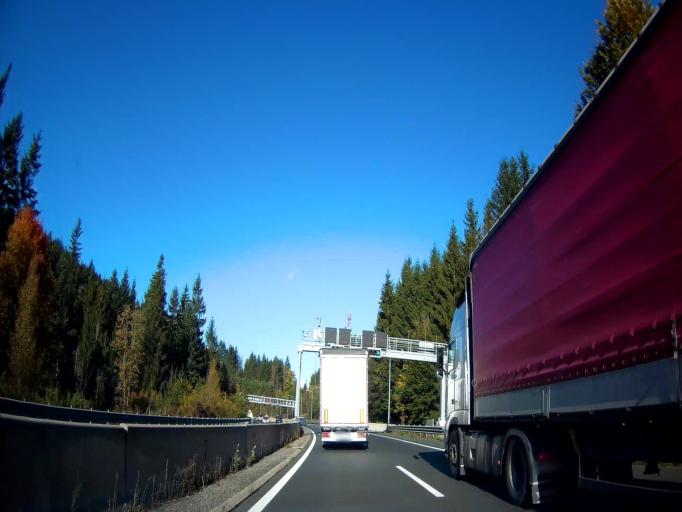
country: AT
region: Carinthia
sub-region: Politischer Bezirk Volkermarkt
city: Griffen
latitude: 46.7039
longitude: 14.7770
